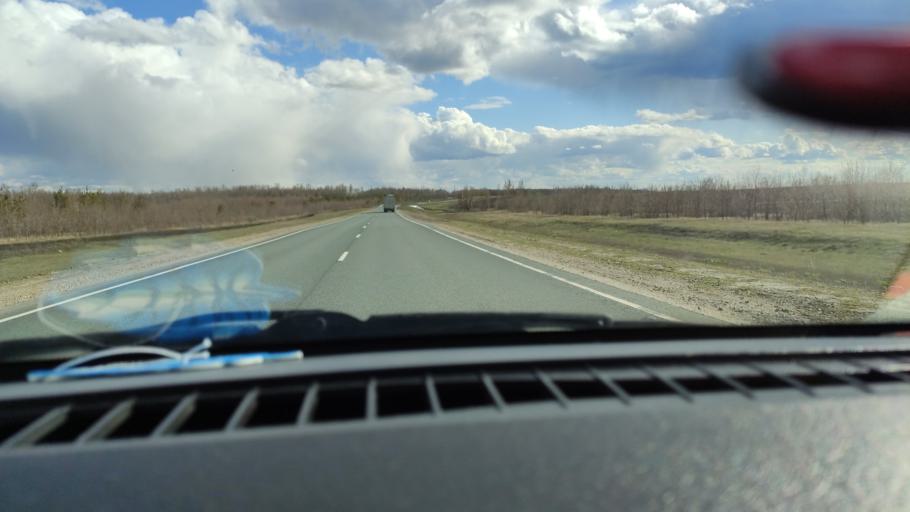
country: RU
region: Saratov
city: Alekseyevka
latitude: 52.2797
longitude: 47.9317
